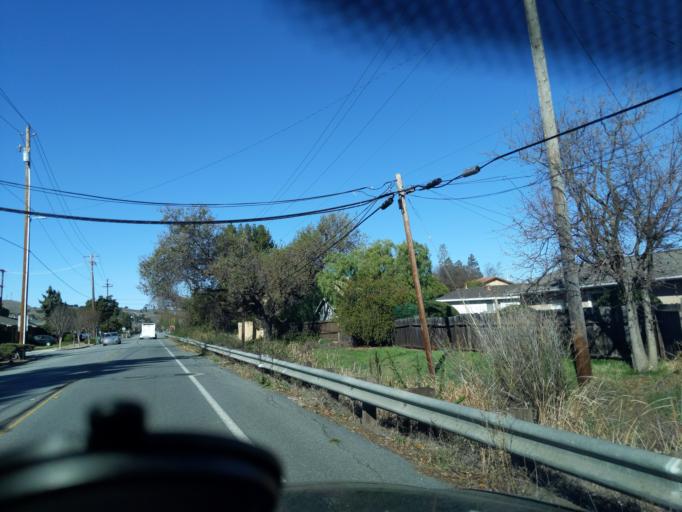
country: US
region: California
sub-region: Santa Clara County
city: Morgan Hill
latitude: 37.1318
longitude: -121.6614
